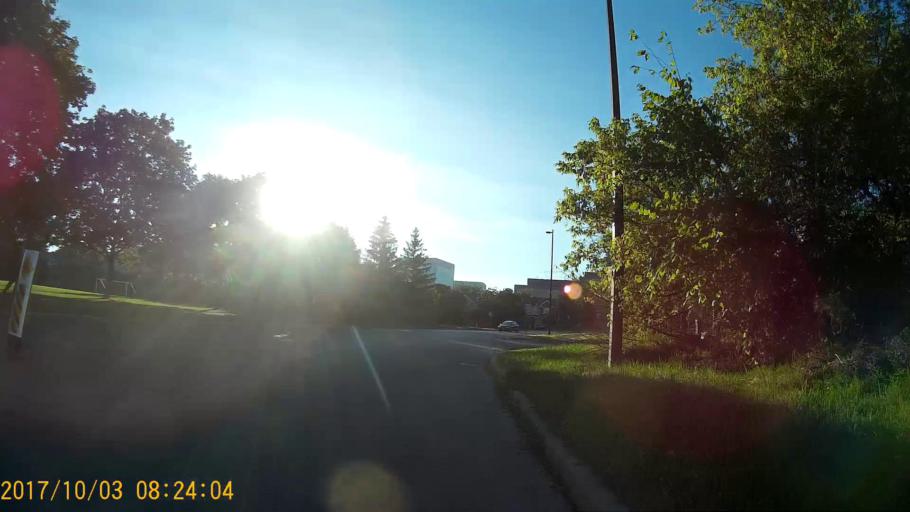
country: CA
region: Ontario
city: Bells Corners
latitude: 45.3508
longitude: -75.9241
